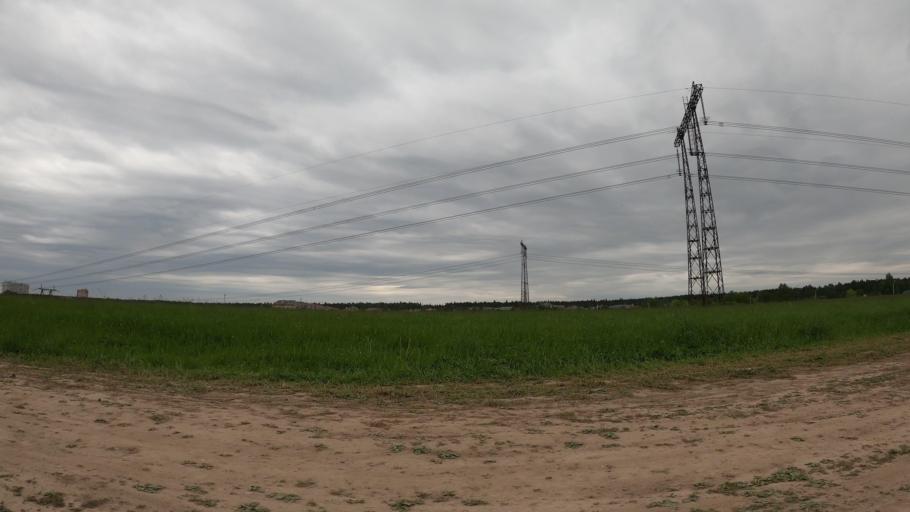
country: RU
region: Moskovskaya
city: Lesnyye Polyany
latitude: 55.9594
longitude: 37.8813
